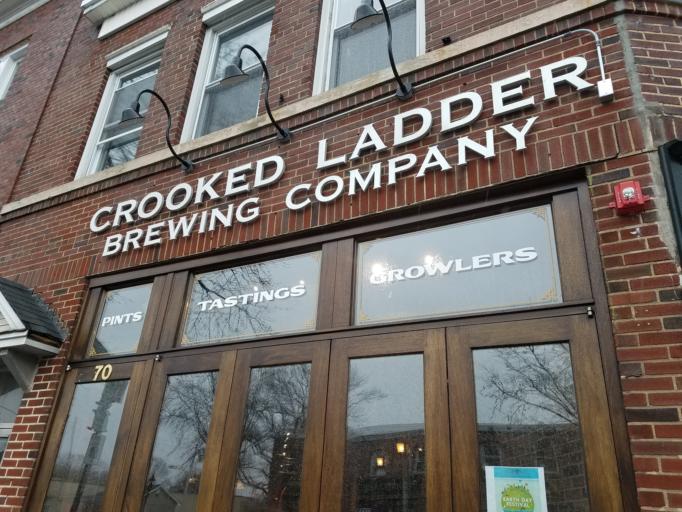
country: US
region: New York
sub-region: Suffolk County
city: Riverhead
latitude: 40.9171
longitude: -72.6635
